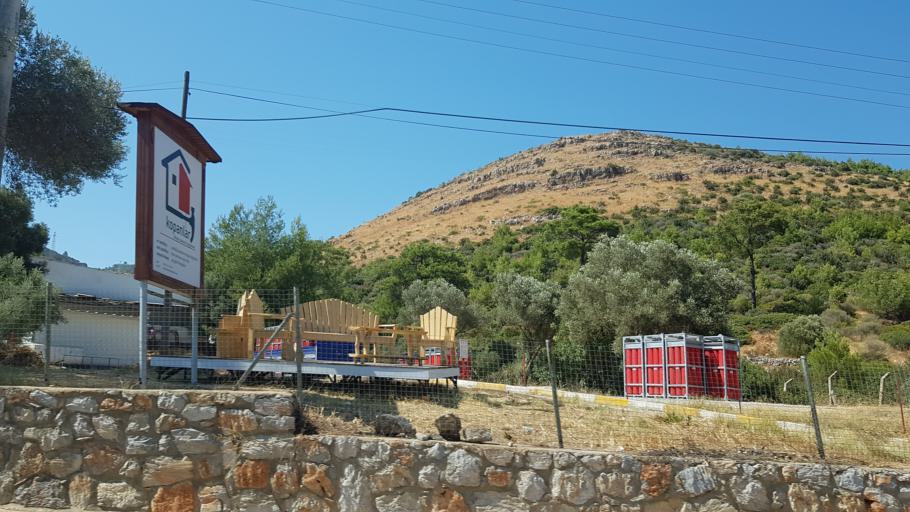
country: TR
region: Mugla
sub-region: Bodrum
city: Bodrum
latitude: 37.0541
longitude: 27.4543
